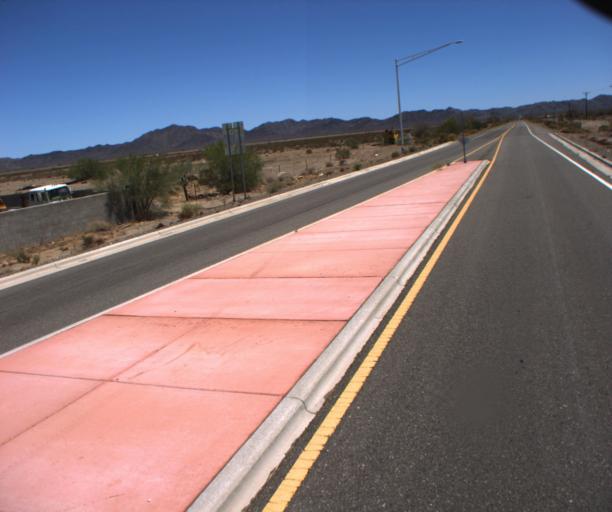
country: US
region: Arizona
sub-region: La Paz County
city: Salome
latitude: 33.7185
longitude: -113.7661
